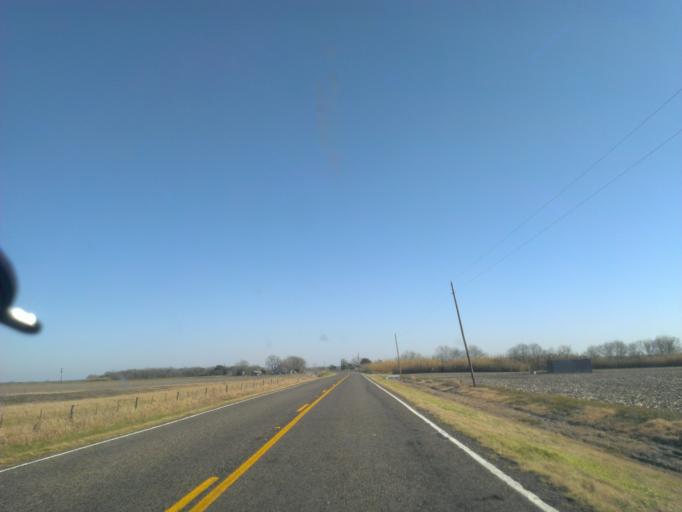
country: US
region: Texas
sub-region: Milam County
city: Thorndale
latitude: 30.5440
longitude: -97.2752
